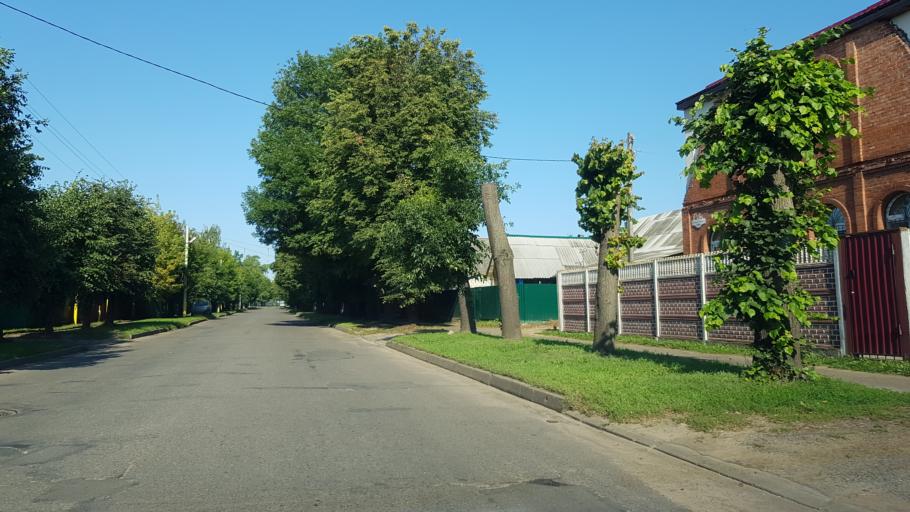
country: BY
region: Mogilev
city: Babruysk
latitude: 53.1351
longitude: 29.1851
